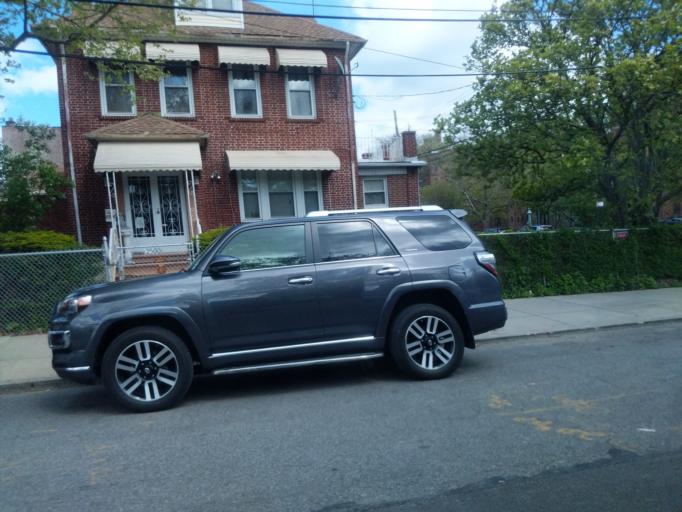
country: US
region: New York
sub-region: Bronx
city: The Bronx
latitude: 40.8632
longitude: -73.8616
